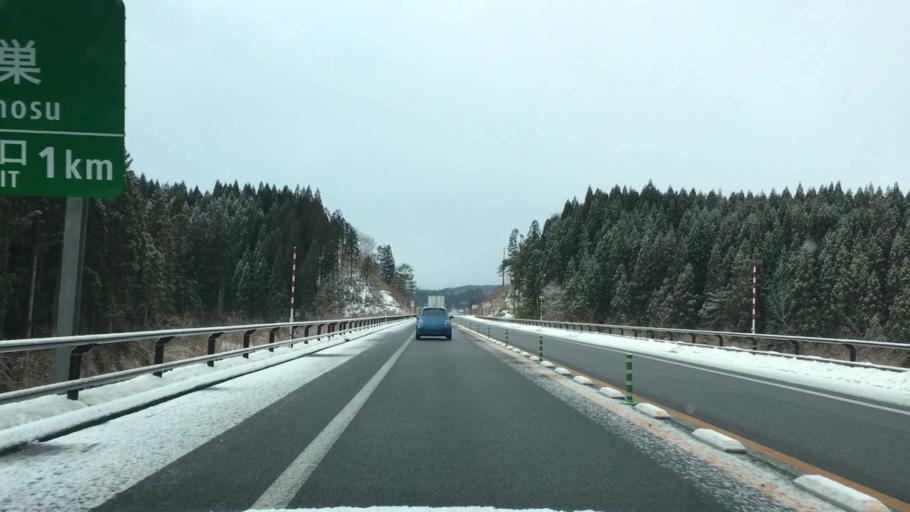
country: JP
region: Akita
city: Takanosu
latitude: 40.2078
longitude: 140.4089
